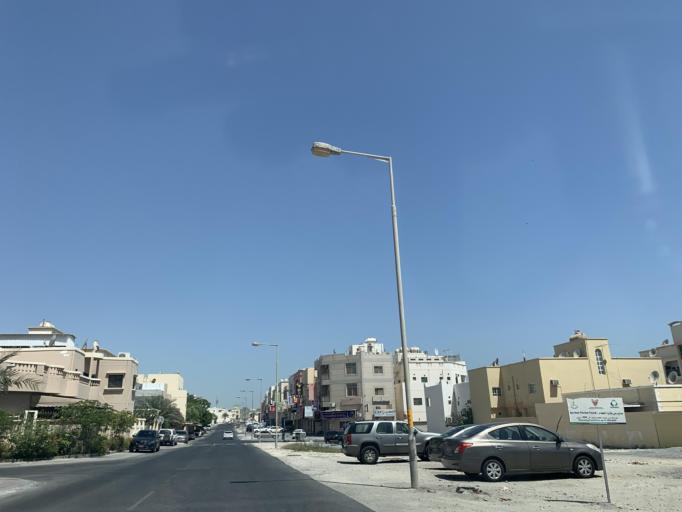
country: BH
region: Northern
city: Ar Rifa'
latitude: 26.1358
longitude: 50.5772
